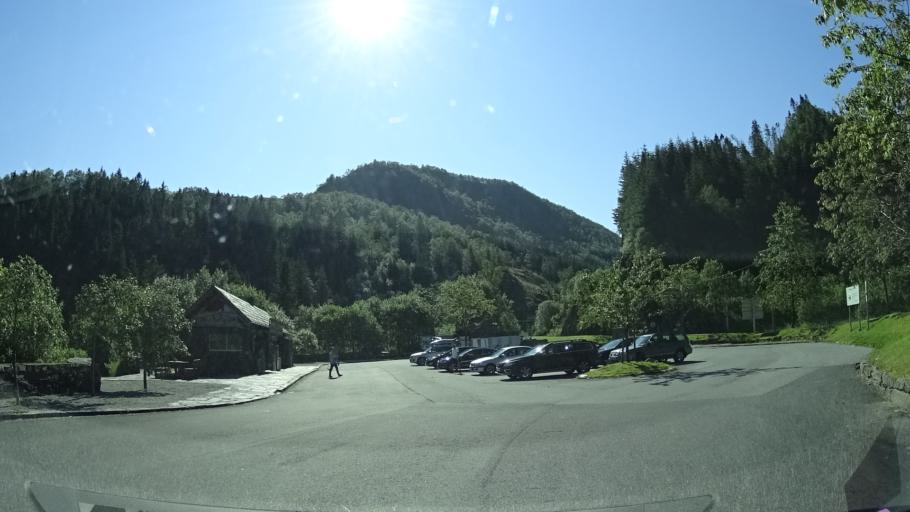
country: NO
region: Hordaland
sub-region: Samnanger
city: Tysse
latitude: 60.4245
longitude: 5.6267
